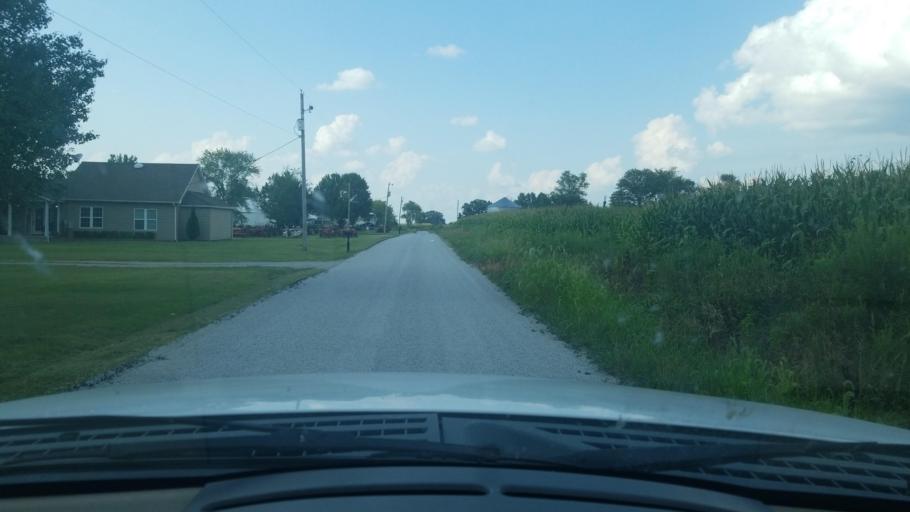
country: US
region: Illinois
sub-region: Saline County
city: Eldorado
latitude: 37.8307
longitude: -88.4386
